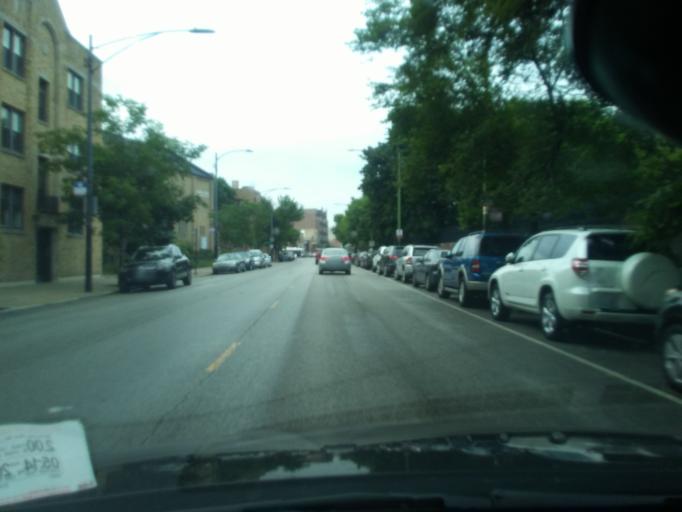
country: US
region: Illinois
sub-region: Cook County
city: Lincolnwood
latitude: 41.9600
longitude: -87.6653
